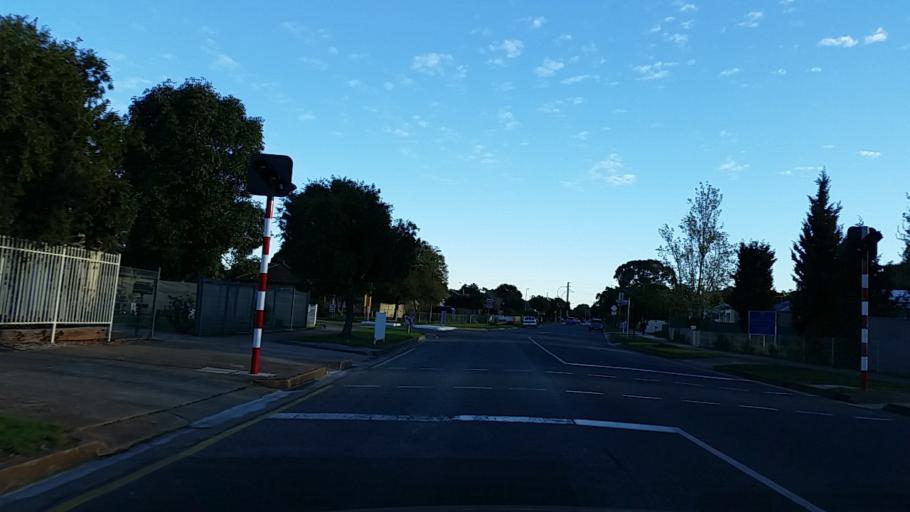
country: AU
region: South Australia
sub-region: Salisbury
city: Elizabeth
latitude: -34.7303
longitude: 138.6603
